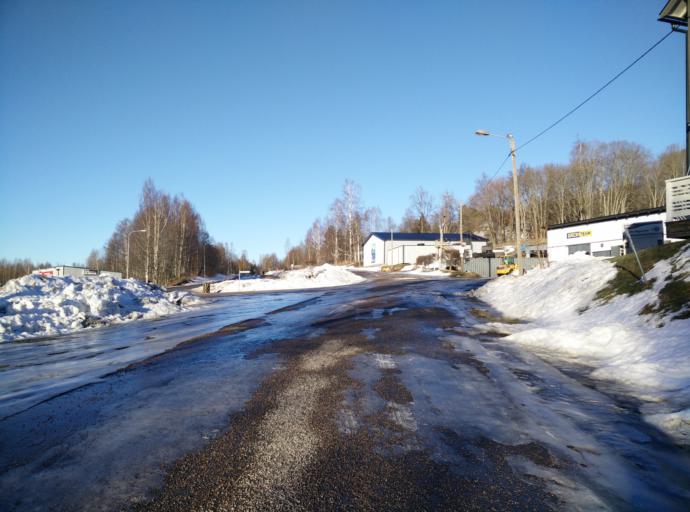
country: SE
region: Vaesternorrland
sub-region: Sundsvalls Kommun
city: Skottsund
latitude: 62.3120
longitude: 17.3929
